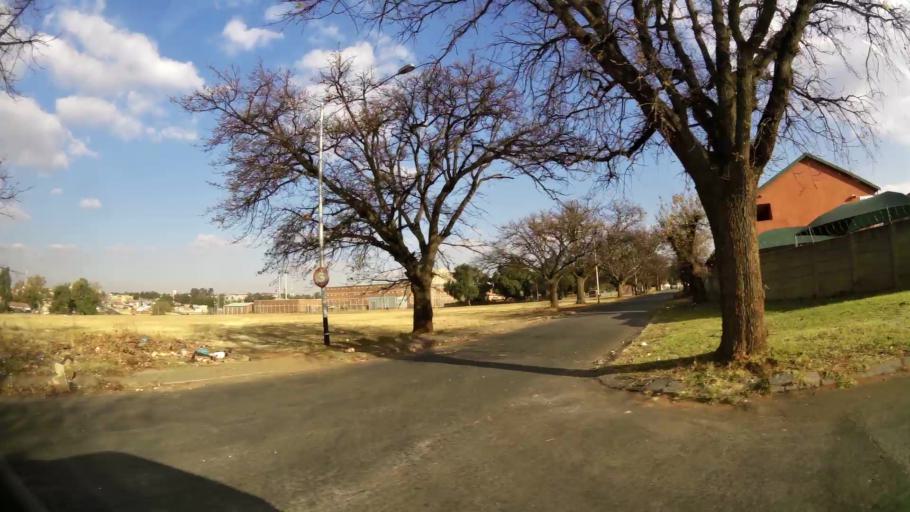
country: ZA
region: Gauteng
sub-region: West Rand District Municipality
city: Krugersdorp
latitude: -26.0992
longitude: 27.7619
